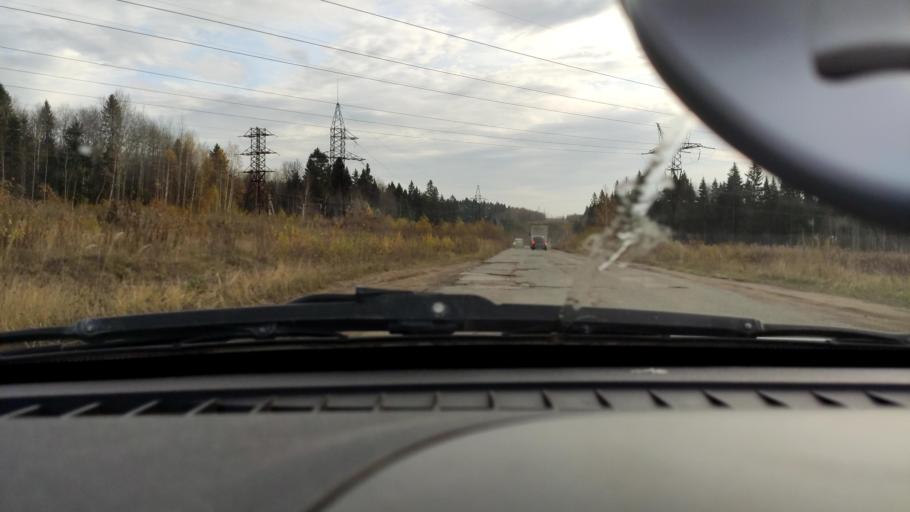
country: RU
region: Perm
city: Perm
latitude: 58.0888
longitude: 56.4205
